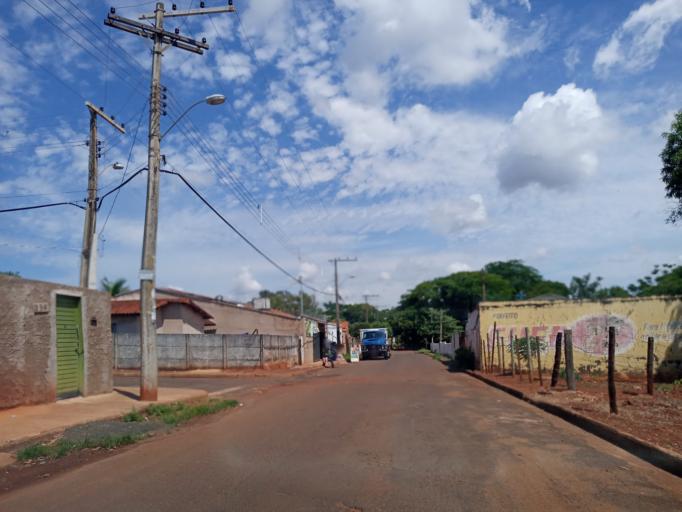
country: BR
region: Minas Gerais
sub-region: Ituiutaba
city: Ituiutaba
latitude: -18.9947
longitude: -49.4739
